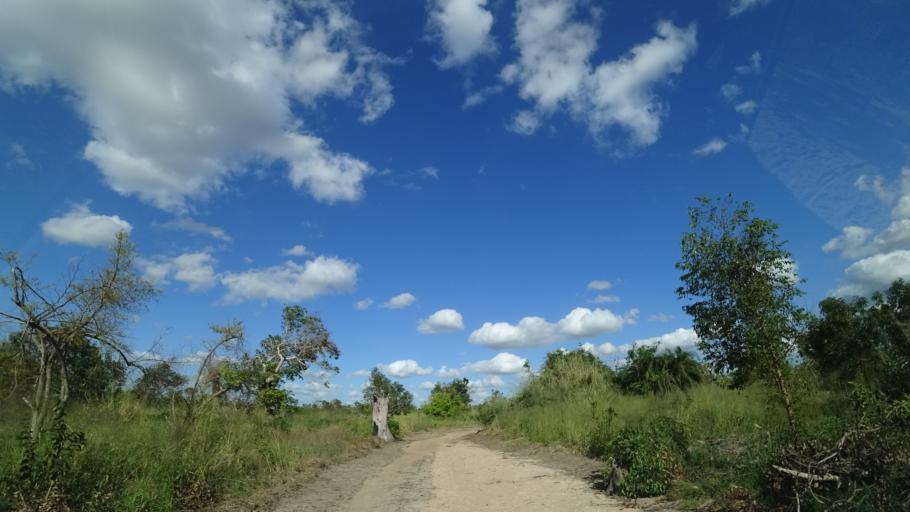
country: MZ
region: Sofala
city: Dondo
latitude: -19.4252
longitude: 34.7228
